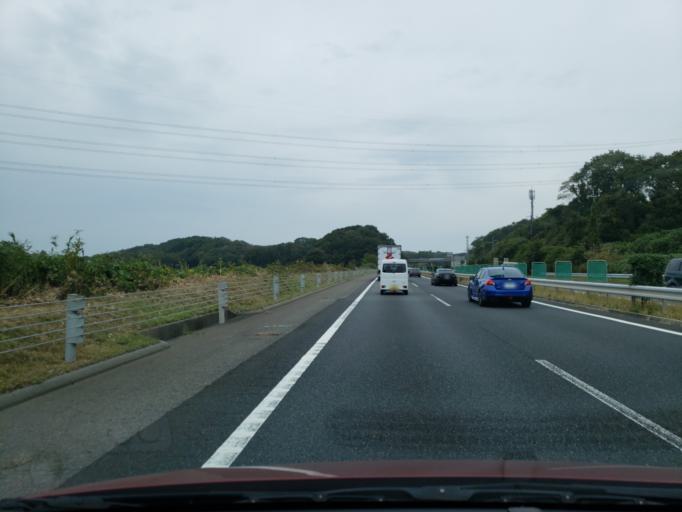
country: JP
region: Hyogo
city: Sandacho
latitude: 34.8326
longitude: 135.1869
